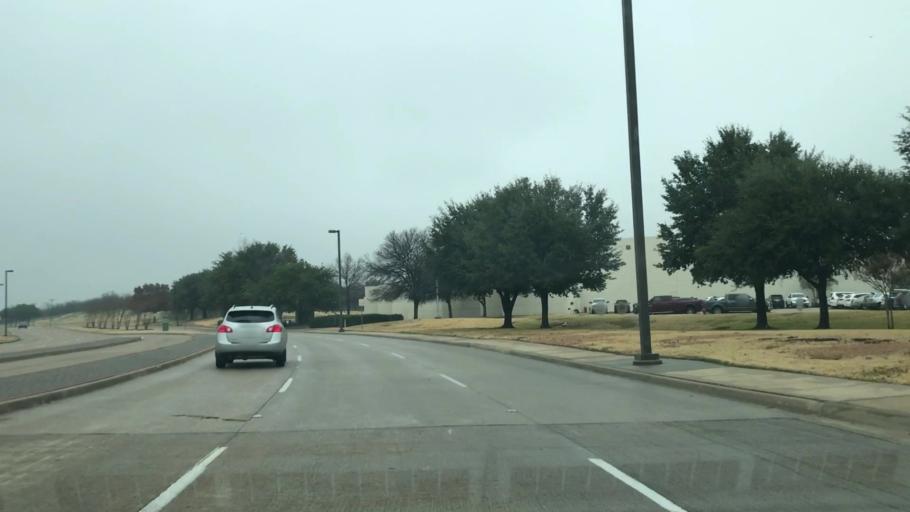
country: US
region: Texas
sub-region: Dallas County
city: Farmers Branch
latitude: 32.8861
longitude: -96.9407
